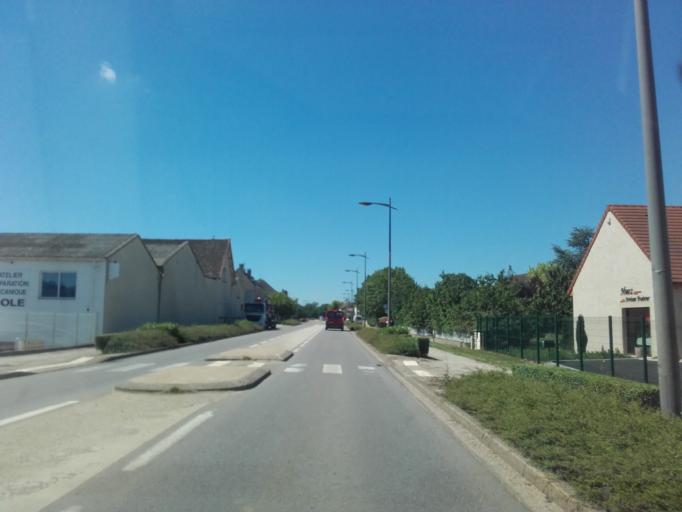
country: FR
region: Bourgogne
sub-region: Departement de la Cote-d'Or
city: Meursault
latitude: 46.9751
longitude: 4.7850
